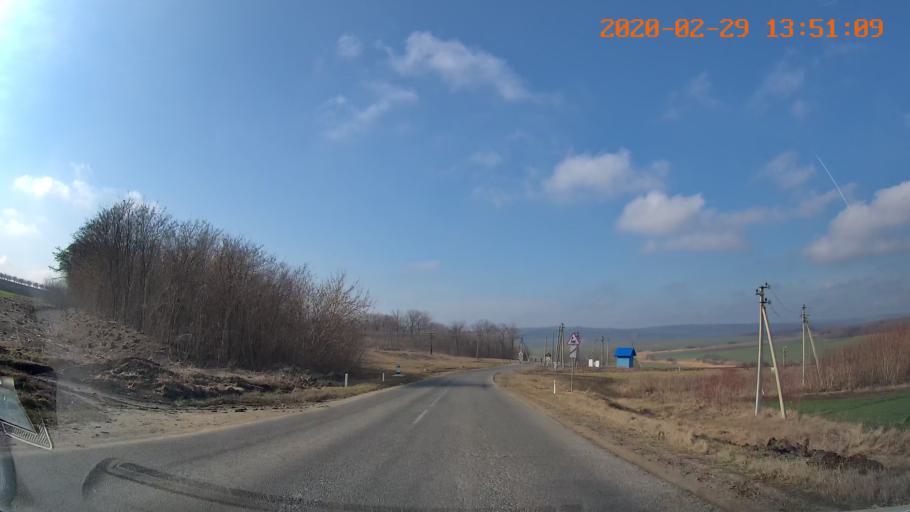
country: MD
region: Floresti
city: Leninskiy
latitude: 47.8412
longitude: 28.4641
